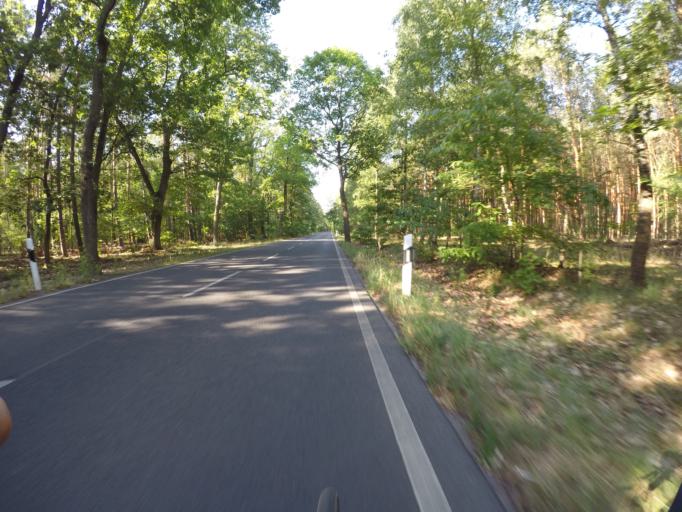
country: DE
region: Berlin
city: Schmockwitz
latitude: 52.3567
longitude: 13.6501
